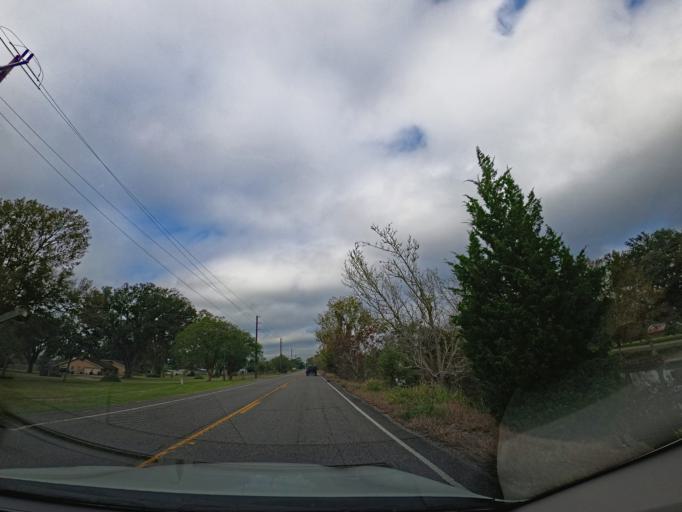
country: US
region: Louisiana
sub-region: Terrebonne Parish
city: Bayou Cane
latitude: 29.6063
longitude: -90.8700
